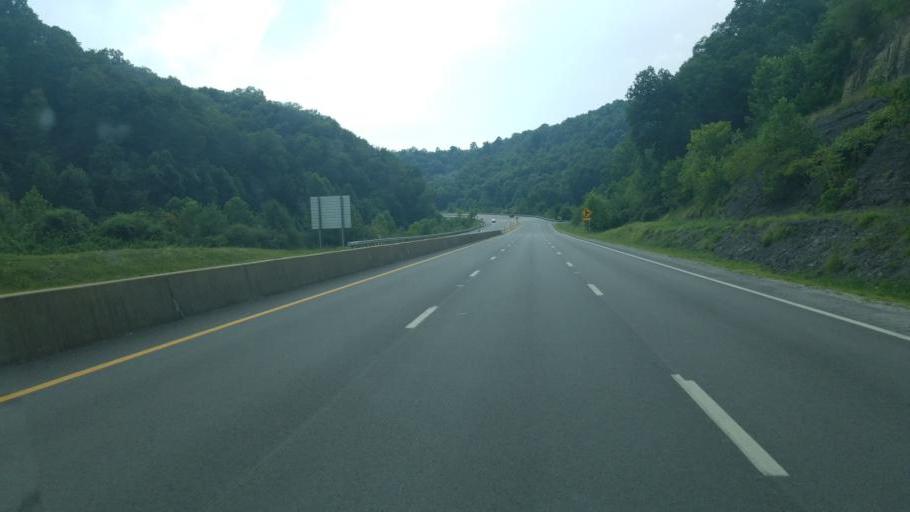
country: US
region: West Virginia
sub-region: Logan County
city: Chapmanville
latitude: 37.9274
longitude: -82.0217
